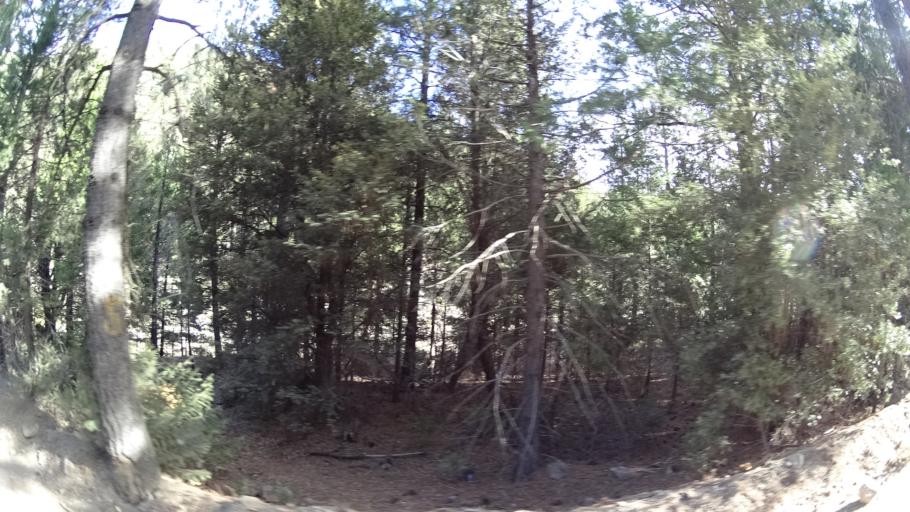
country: US
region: California
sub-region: Siskiyou County
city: Yreka
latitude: 41.7157
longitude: -122.7910
